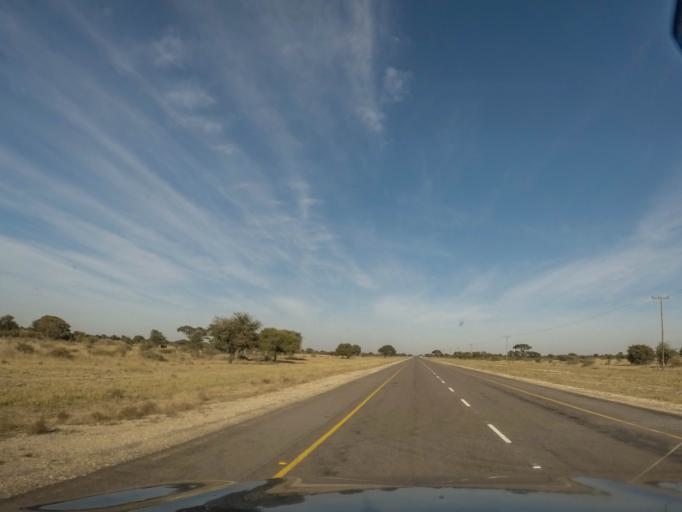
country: BW
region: South East
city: Janeng
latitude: -25.5543
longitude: 25.3171
